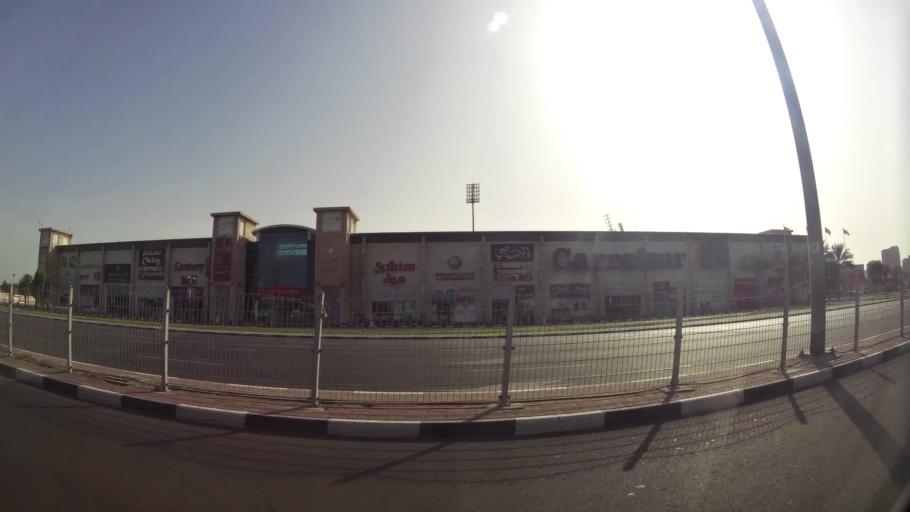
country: AE
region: Ash Shariqah
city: Sharjah
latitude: 25.2892
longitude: 55.3466
